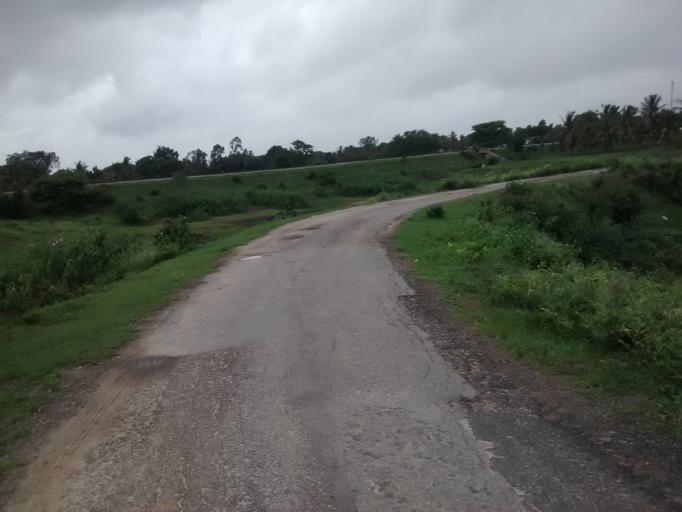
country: IN
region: Karnataka
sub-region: Hassan
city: Hassan
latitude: 12.9497
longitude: 76.1450
